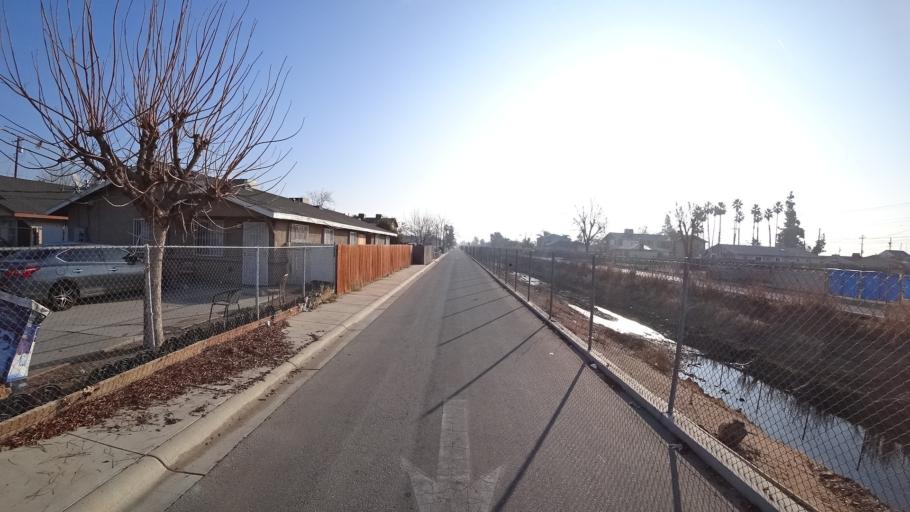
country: US
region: California
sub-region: Kern County
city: Bakersfield
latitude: 35.3781
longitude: -118.9839
